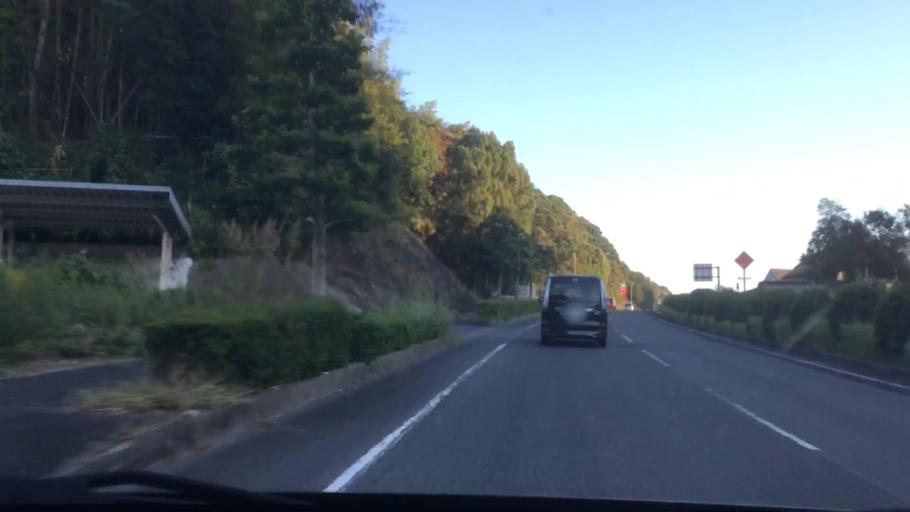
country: JP
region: Nagasaki
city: Sasebo
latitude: 33.1390
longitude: 129.7850
